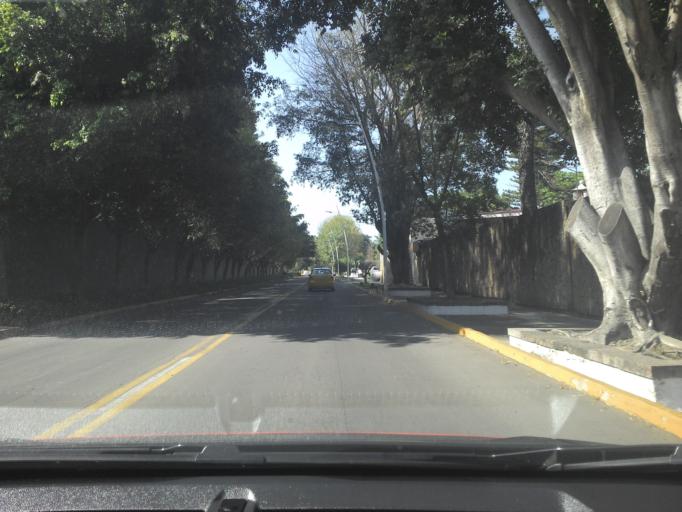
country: MX
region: Jalisco
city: Zapopan2
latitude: 20.6947
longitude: -103.4008
